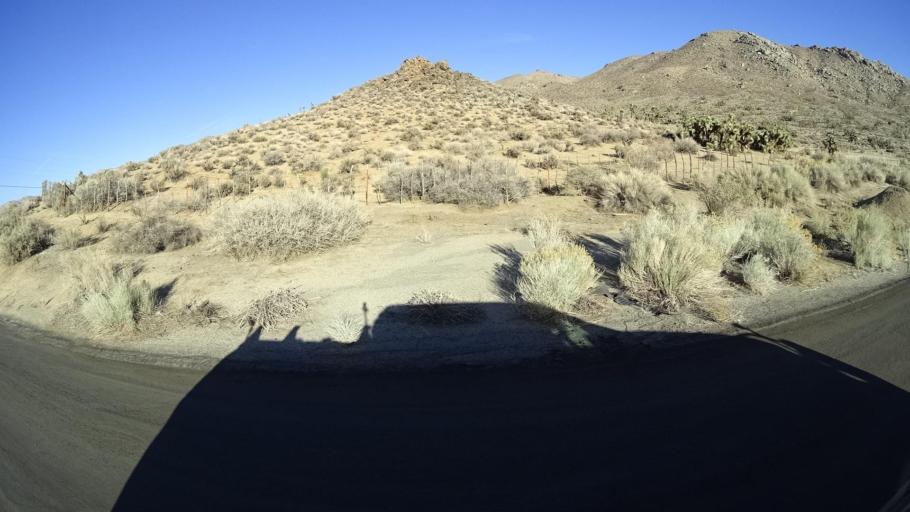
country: US
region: California
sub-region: Kern County
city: Weldon
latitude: 35.5145
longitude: -118.2039
